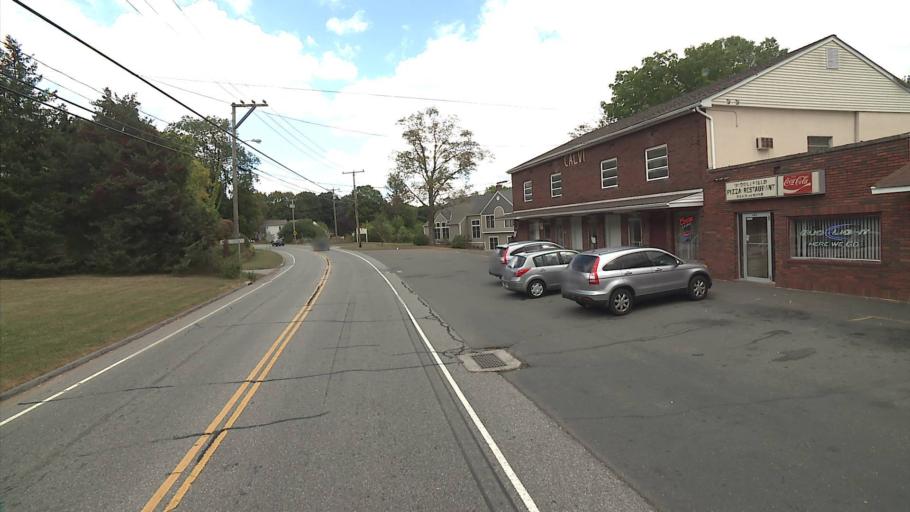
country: US
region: Connecticut
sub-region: Middlesex County
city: Durham
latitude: 41.5128
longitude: -72.7125
